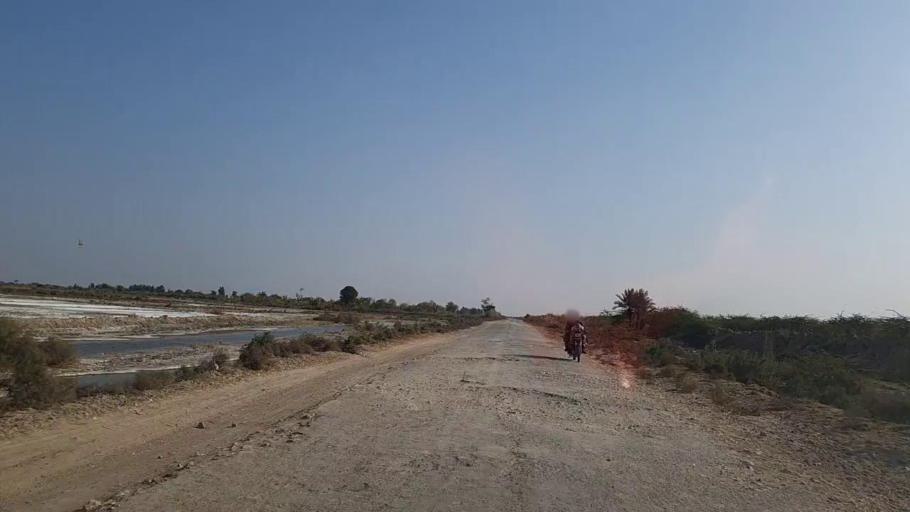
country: PK
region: Sindh
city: Tando Mittha Khan
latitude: 25.9241
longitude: 69.0677
